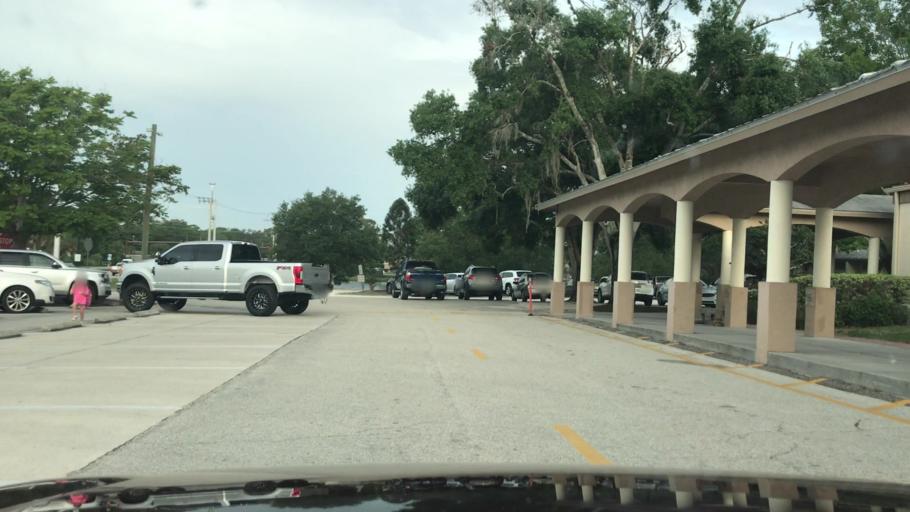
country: US
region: Florida
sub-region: Sarasota County
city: Fruitville
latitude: 27.3235
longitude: -82.4612
